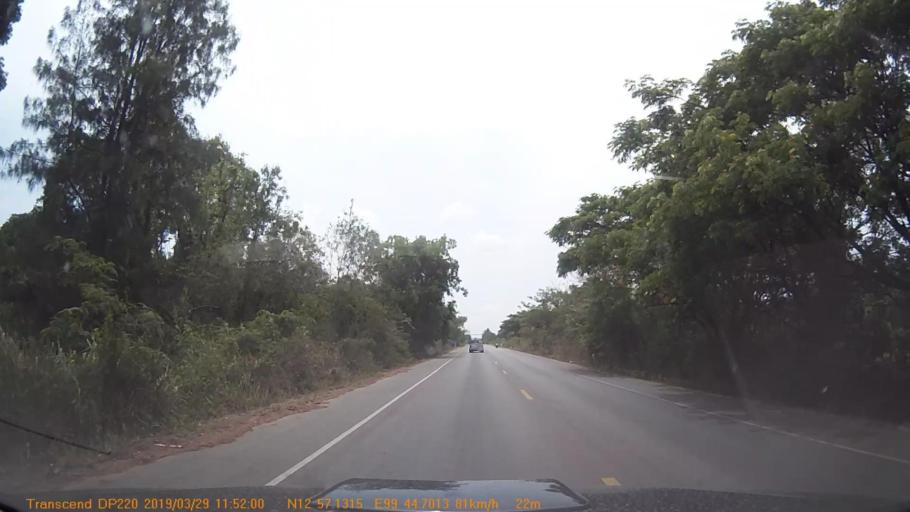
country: TH
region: Phetchaburi
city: Kaeng Krachan
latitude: 12.9520
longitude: 99.7451
